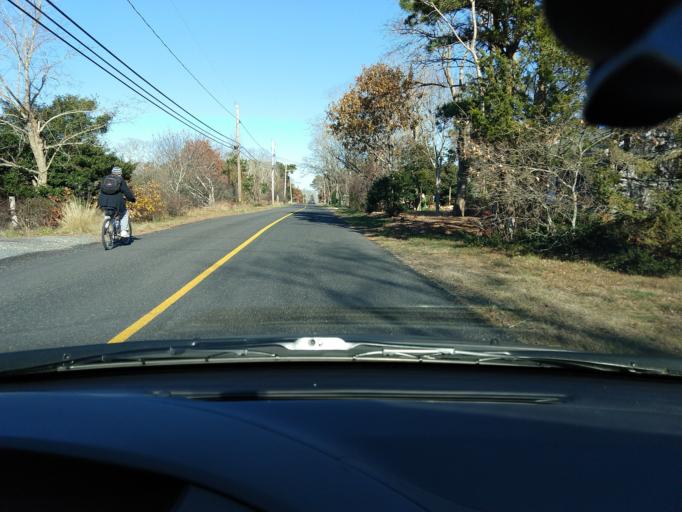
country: US
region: Massachusetts
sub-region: Barnstable County
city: North Eastham
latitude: 41.8728
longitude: -69.9956
